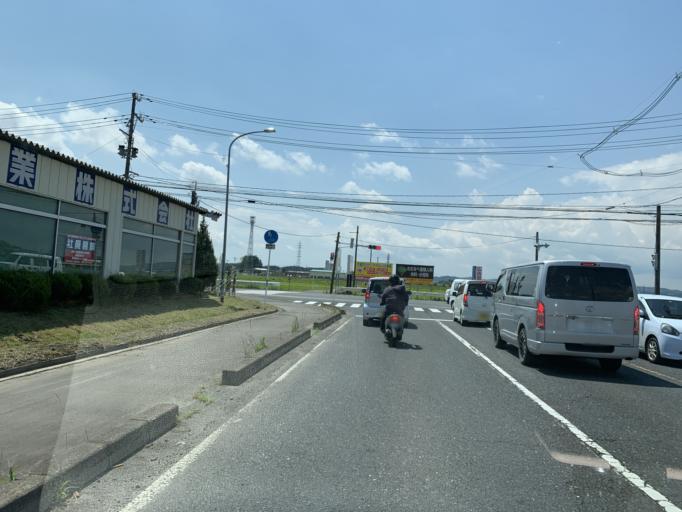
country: JP
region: Miyagi
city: Kogota
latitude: 38.5602
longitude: 141.0441
